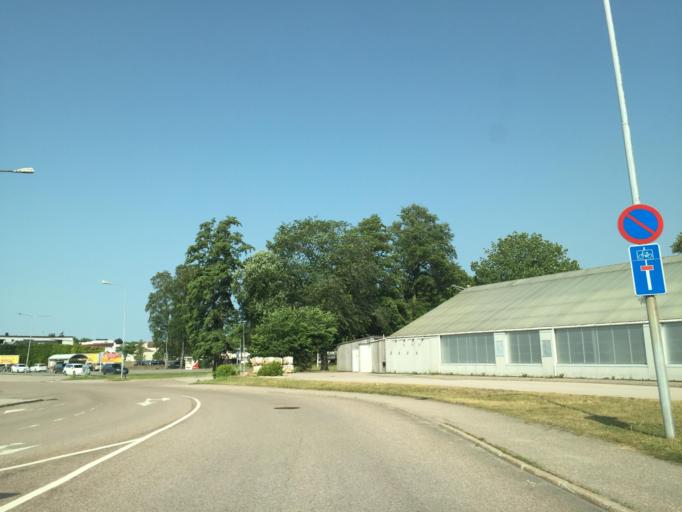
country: SE
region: Vaestra Goetaland
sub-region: Vanersborgs Kommun
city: Vanersborg
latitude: 58.3799
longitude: 12.3170
